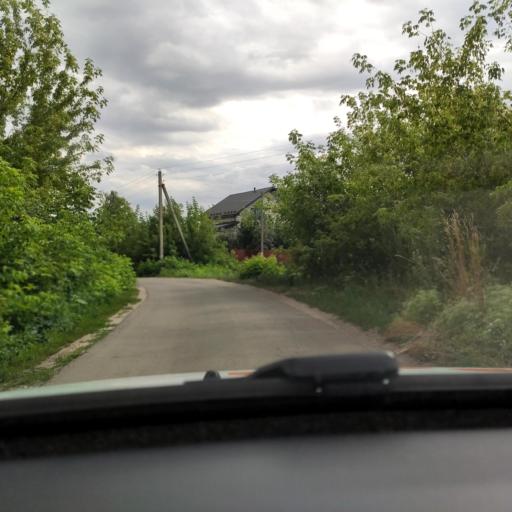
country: RU
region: Voronezj
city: Orlovo
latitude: 51.6499
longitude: 39.5701
